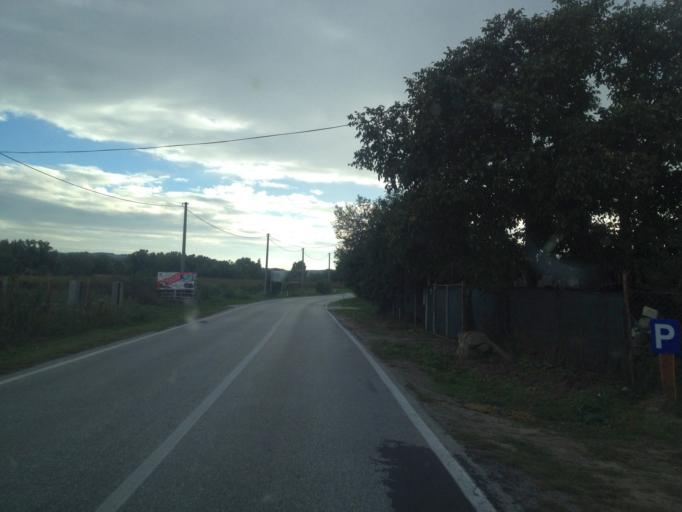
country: HU
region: Komarom-Esztergom
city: Neszmely
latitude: 47.7569
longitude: 18.3964
